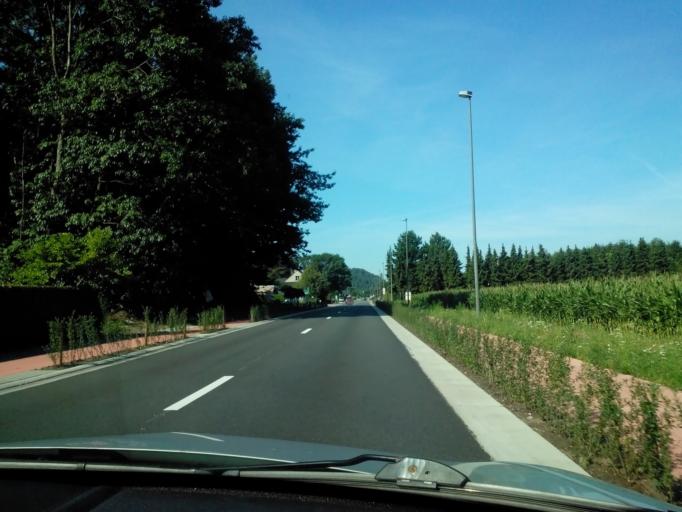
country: BE
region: Flanders
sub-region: Provincie Limburg
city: Opglabbeek
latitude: 51.0329
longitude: 5.5484
